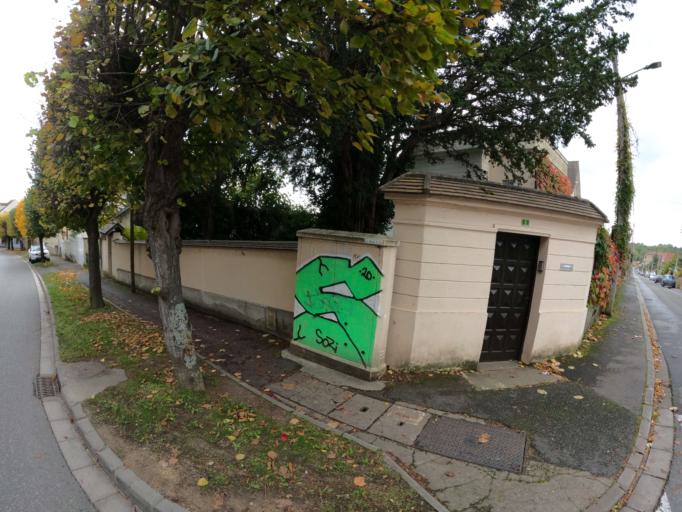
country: FR
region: Ile-de-France
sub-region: Departement de Seine-et-Marne
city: Esbly
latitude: 48.9048
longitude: 2.8099
